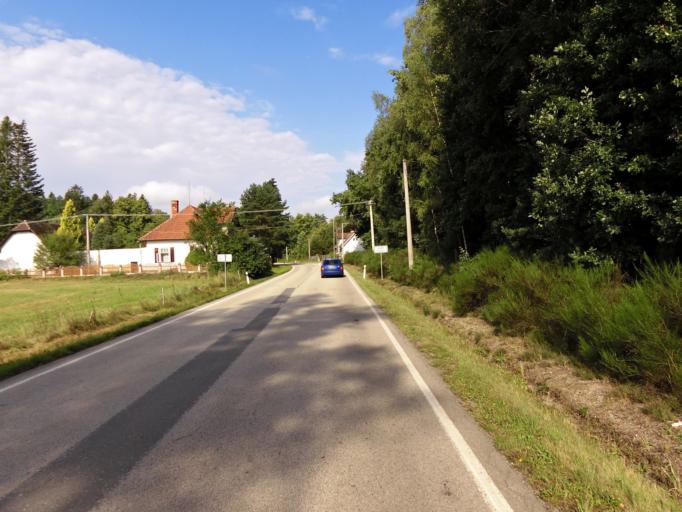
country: CZ
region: Jihocesky
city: Chlum u Trebone
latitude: 48.9502
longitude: 14.8919
